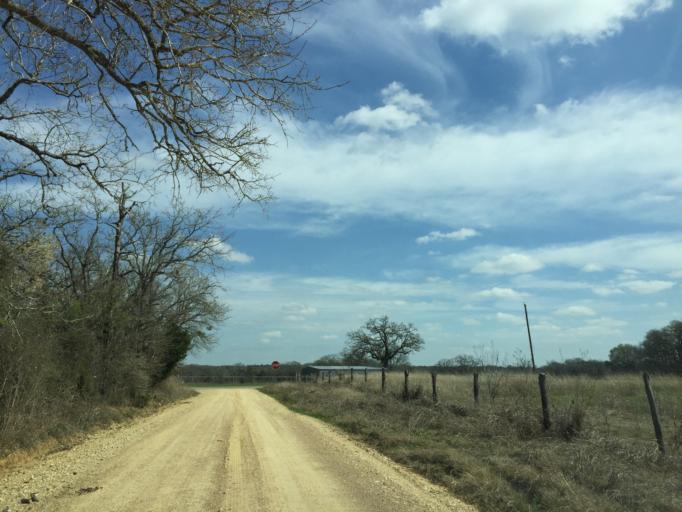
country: US
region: Texas
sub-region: Milam County
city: Thorndale
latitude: 30.5565
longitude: -97.1794
